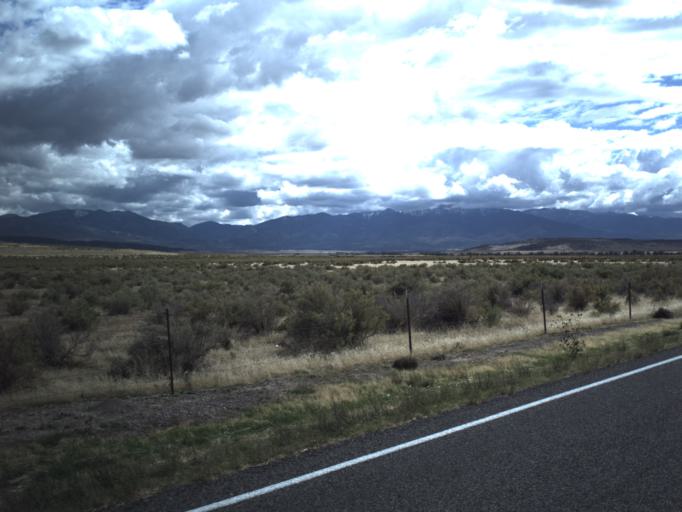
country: US
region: Utah
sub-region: Millard County
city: Fillmore
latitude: 39.0748
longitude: -112.4099
